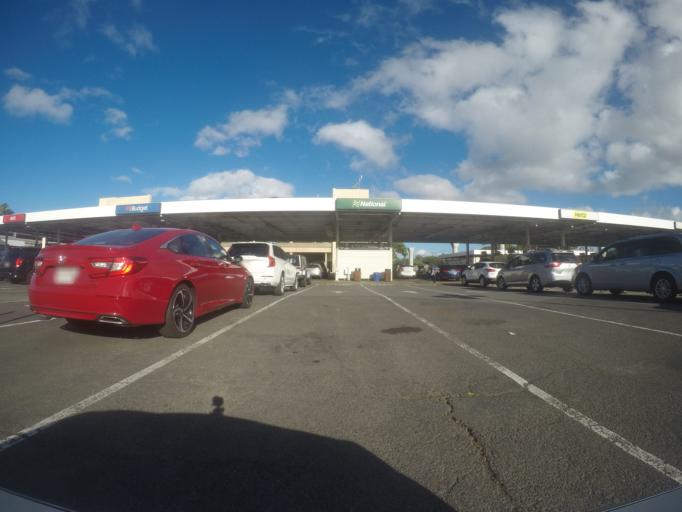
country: US
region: Hawaii
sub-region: Honolulu County
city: Hickam Field
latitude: 21.3331
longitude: -157.9180
